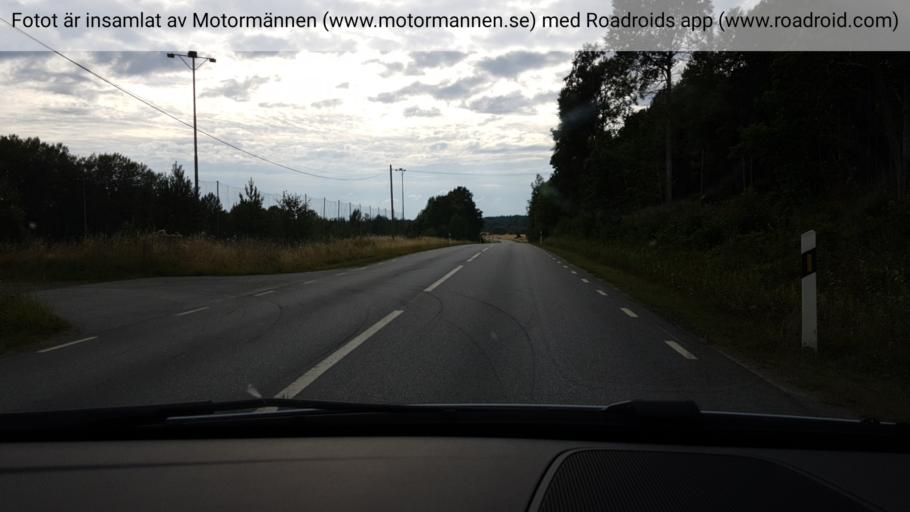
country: SE
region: Stockholm
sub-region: Norrtalje Kommun
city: Skanninge
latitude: 59.8950
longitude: 18.4502
